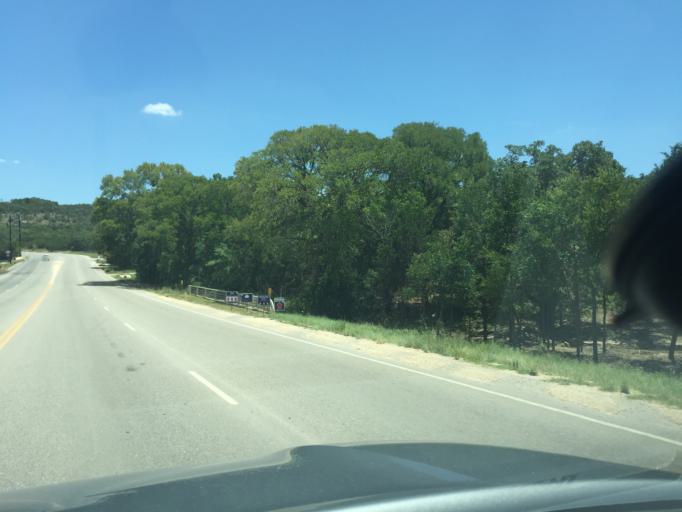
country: US
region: Texas
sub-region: Bexar County
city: Timberwood Park
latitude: 29.7139
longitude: -98.4690
